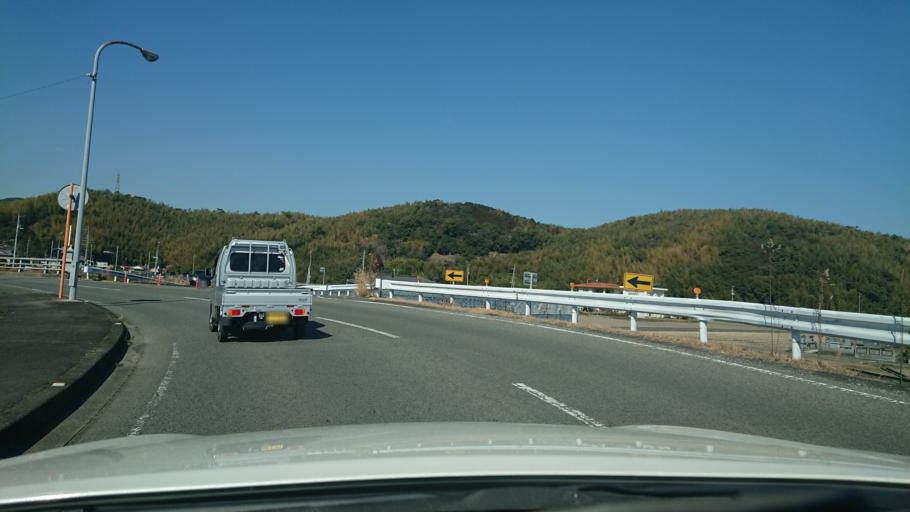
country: JP
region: Tokushima
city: Komatsushimacho
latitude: 33.9698
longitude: 134.6014
